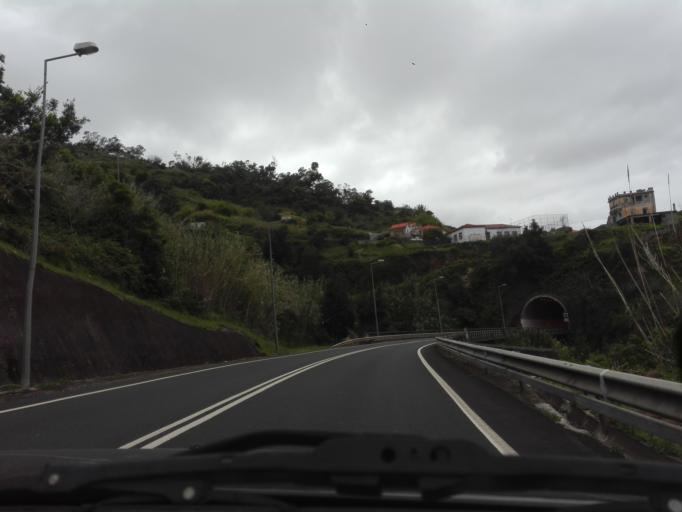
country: PT
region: Madeira
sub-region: Santana
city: Santana
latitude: 32.7561
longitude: -16.8275
